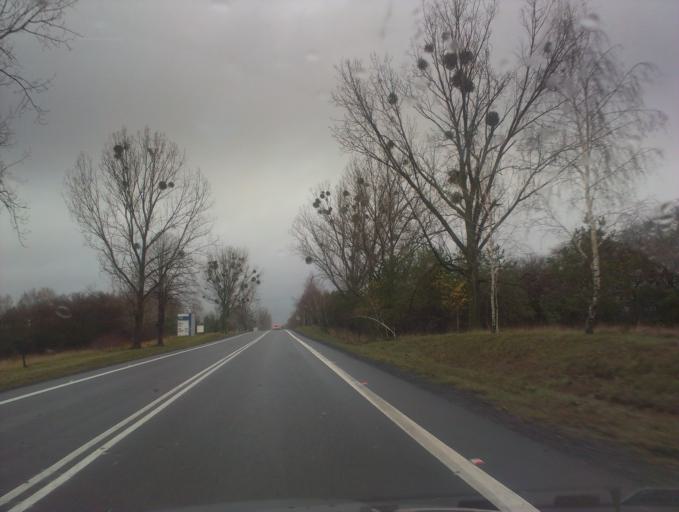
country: PL
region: Greater Poland Voivodeship
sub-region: Powiat poznanski
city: Zlotniki
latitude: 52.5370
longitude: 16.8365
